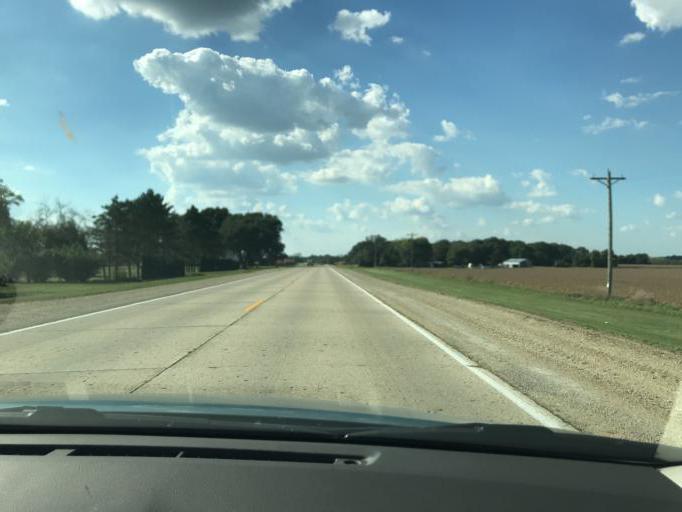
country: US
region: Wisconsin
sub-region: Green County
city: Brodhead
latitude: 42.5671
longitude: -89.3384
